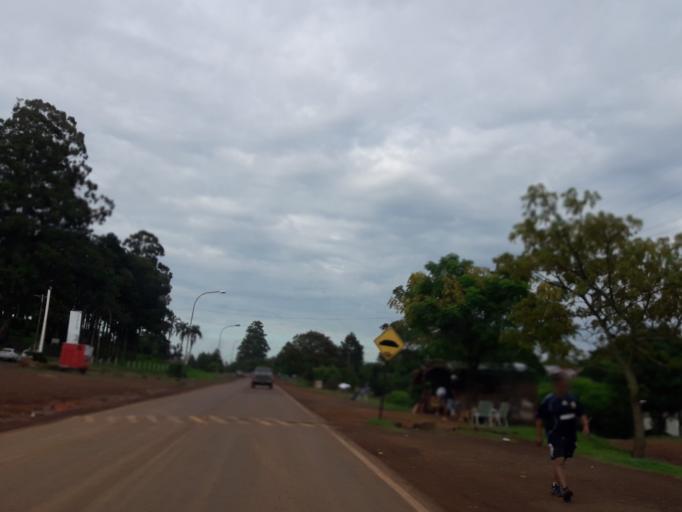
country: AR
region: Misiones
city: Bernardo de Irigoyen
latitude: -26.2620
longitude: -53.6504
